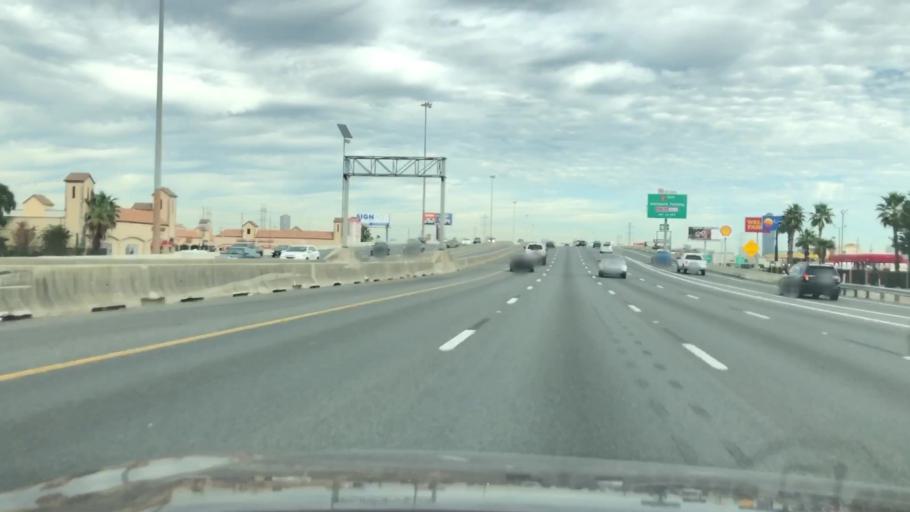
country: US
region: Texas
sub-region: Harris County
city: Bellaire
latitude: 29.7150
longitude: -95.5010
